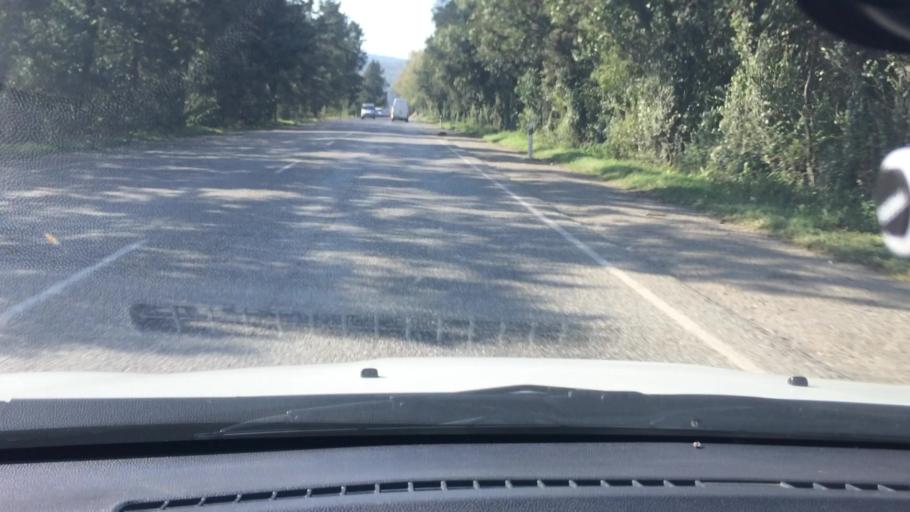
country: GE
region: Imereti
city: Samtredia
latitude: 42.1229
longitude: 42.3332
